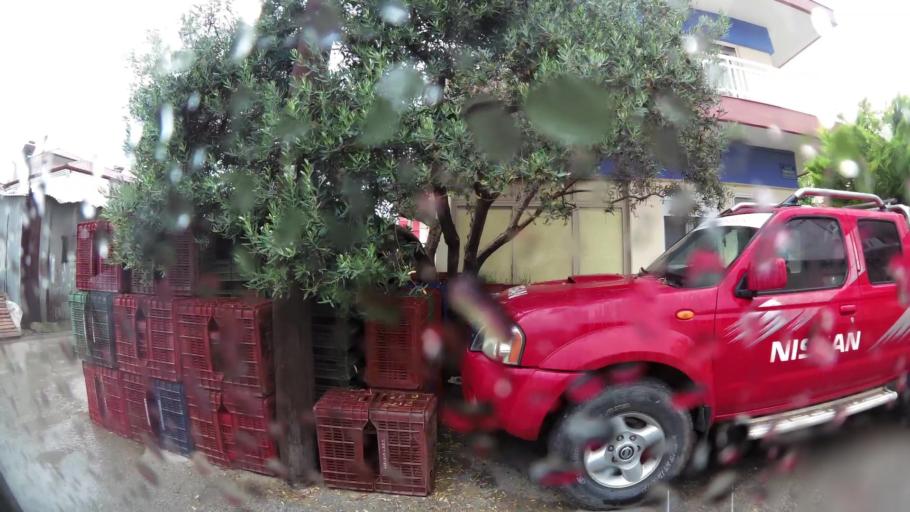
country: GR
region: Central Macedonia
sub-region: Nomos Imathias
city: Veroia
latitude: 40.5334
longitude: 22.2035
